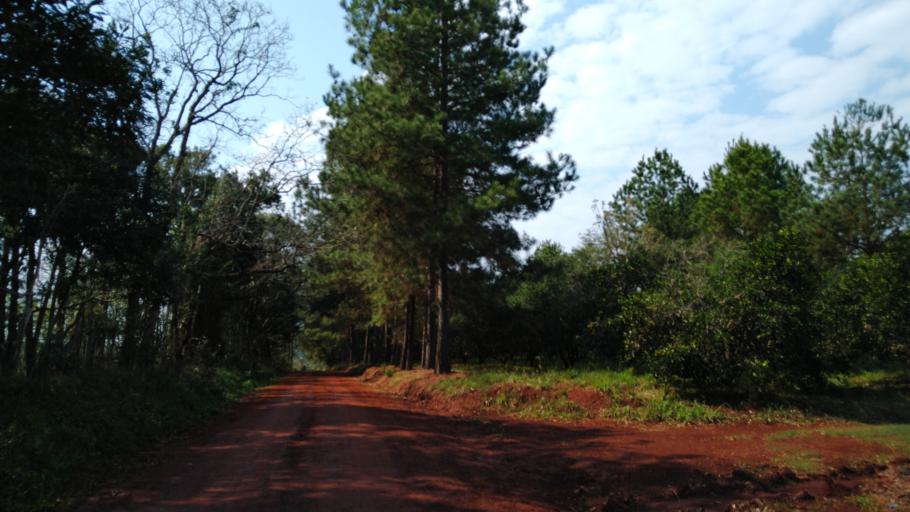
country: AR
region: Misiones
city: Capiovi
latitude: -26.9529
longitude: -55.0467
